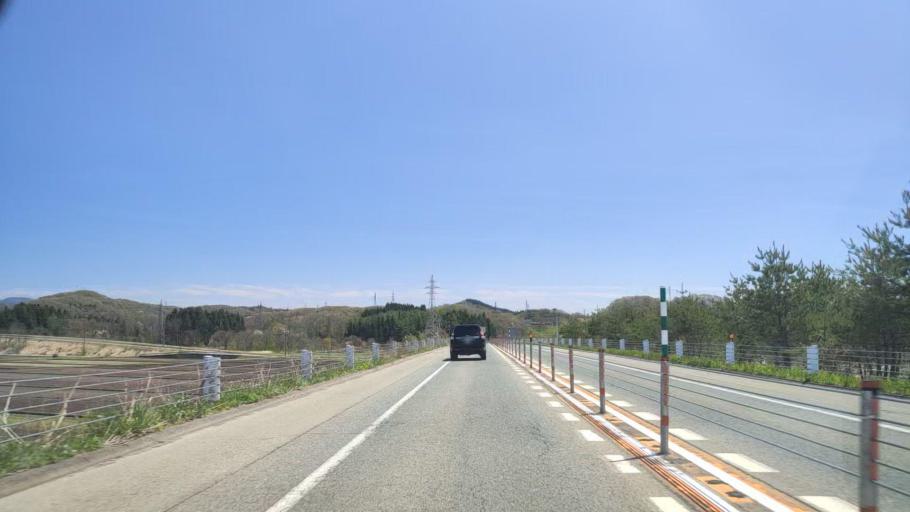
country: JP
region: Yamagata
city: Shinjo
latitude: 38.7322
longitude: 140.3036
